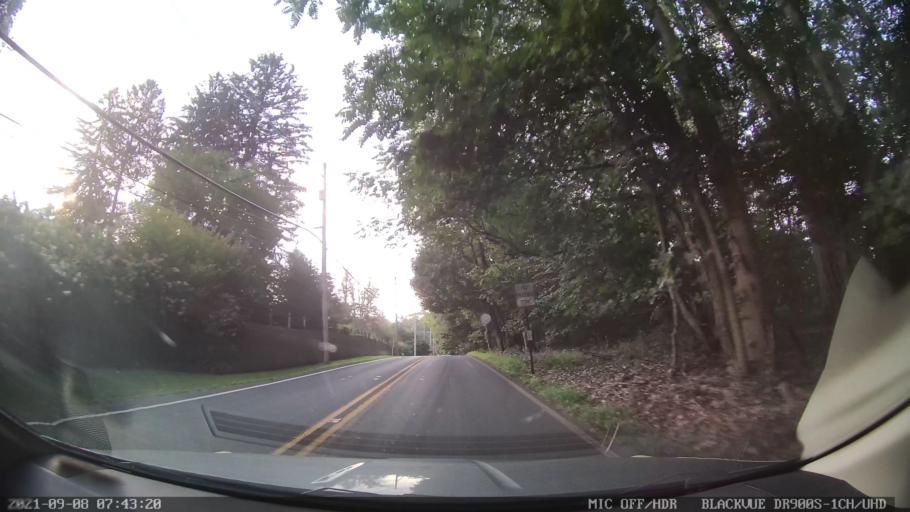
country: US
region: Pennsylvania
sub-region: Montgomery County
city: King of Prussia
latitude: 40.0699
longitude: -75.3788
